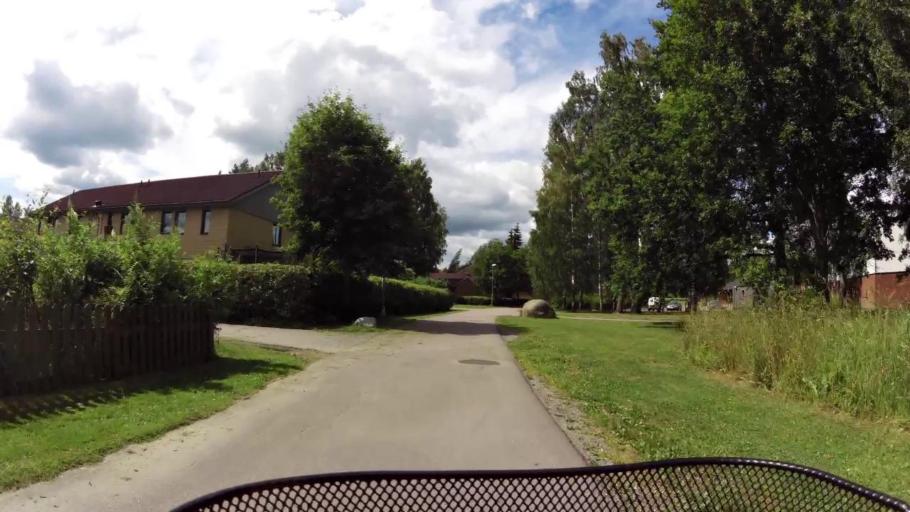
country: SE
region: OEstergoetland
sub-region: Linkopings Kommun
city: Malmslatt
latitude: 58.4226
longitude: 15.5090
